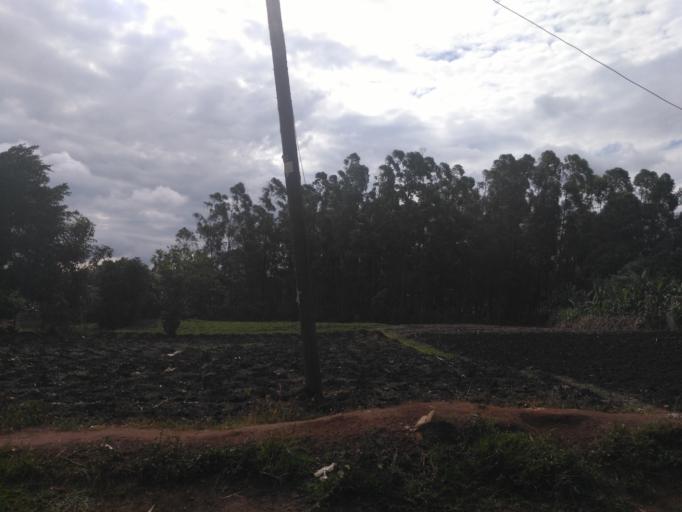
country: UG
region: Central Region
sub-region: Buikwe District
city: Njeru
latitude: 0.3923
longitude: 33.1703
